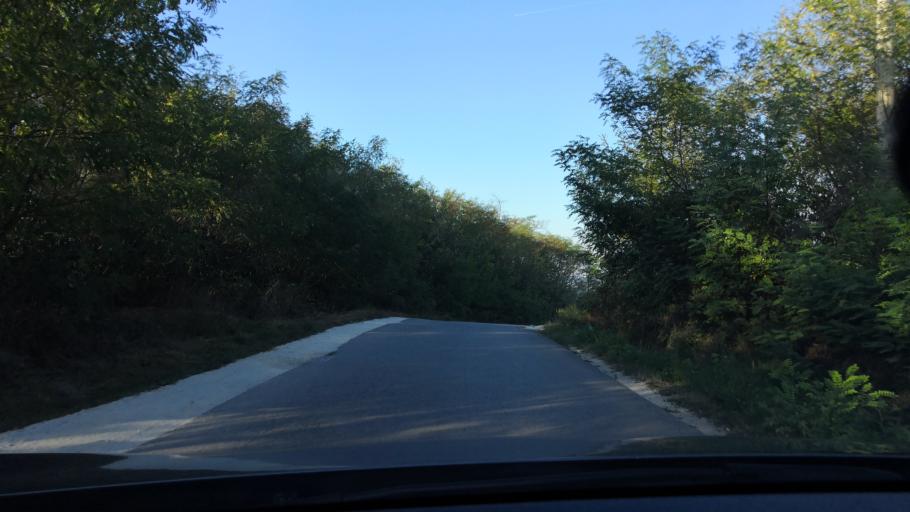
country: RS
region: Central Serbia
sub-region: Sumadijski Okrug
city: Arangelovac
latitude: 44.3307
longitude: 20.5625
